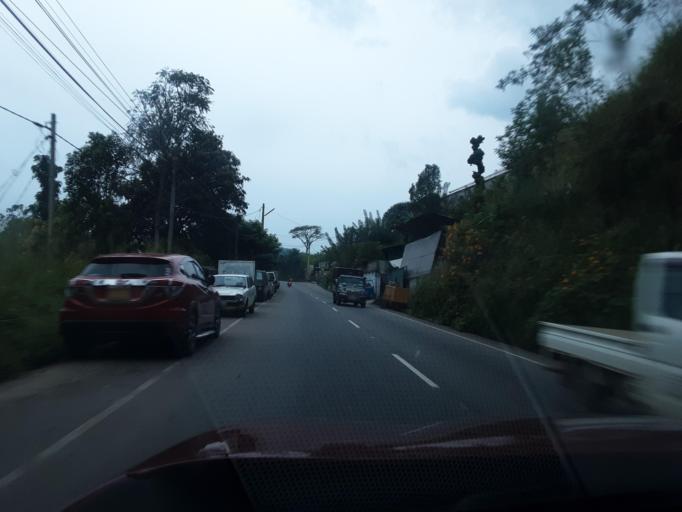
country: LK
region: Central
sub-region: Nuwara Eliya District
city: Nuwara Eliya
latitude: 6.9018
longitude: 80.9049
